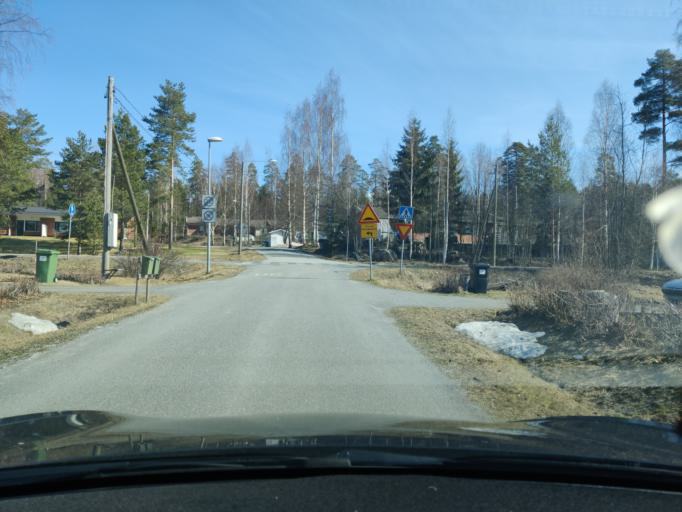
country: FI
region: Northern Savo
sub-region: Kuopio
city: Vehmersalmi
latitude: 62.7659
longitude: 28.0170
